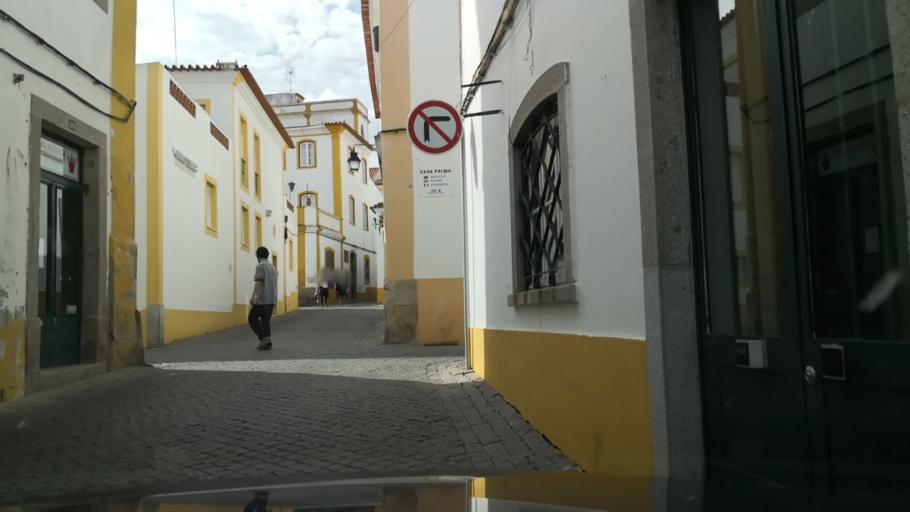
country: PT
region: Evora
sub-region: Evora
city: Evora
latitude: 38.5698
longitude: -7.9097
